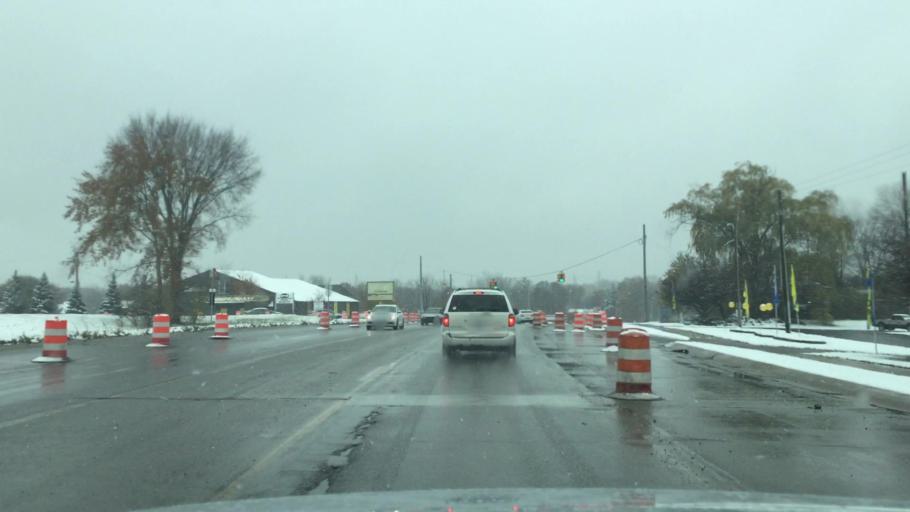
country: US
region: Michigan
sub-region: Oakland County
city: Auburn Hills
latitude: 42.6721
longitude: -83.2538
